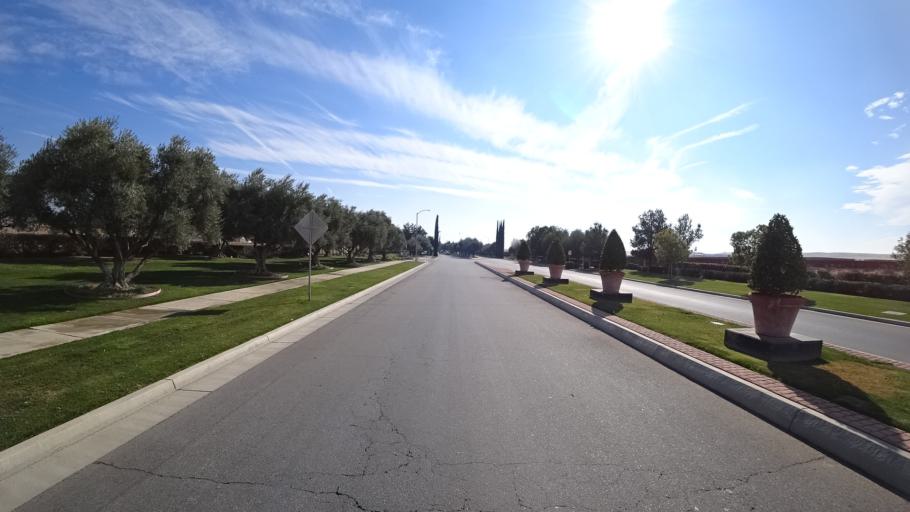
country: US
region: California
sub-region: Kern County
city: Oildale
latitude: 35.4008
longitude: -118.8911
